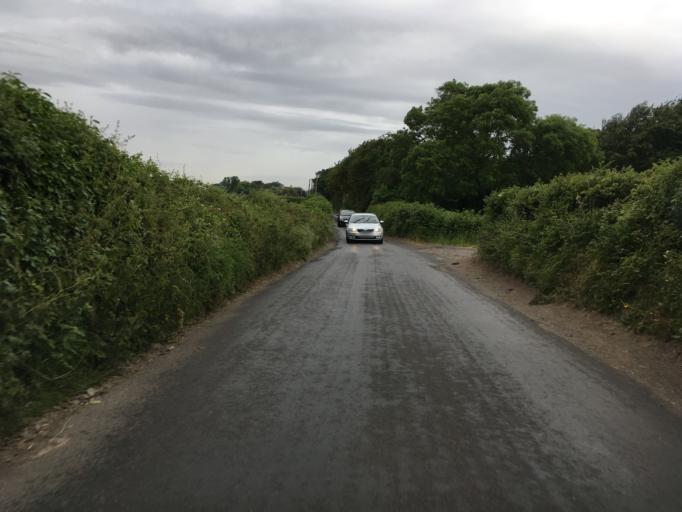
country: GB
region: England
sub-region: North Somerset
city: Brockley
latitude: 51.4145
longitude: -2.7894
